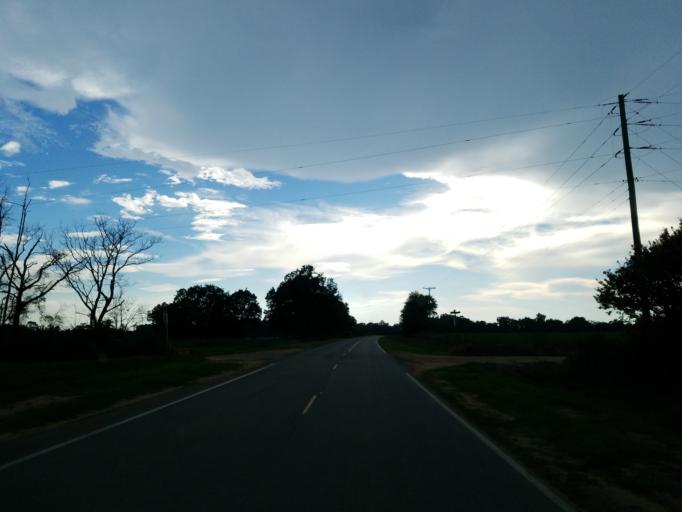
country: US
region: Georgia
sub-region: Tift County
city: Omega
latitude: 31.2572
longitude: -83.5365
